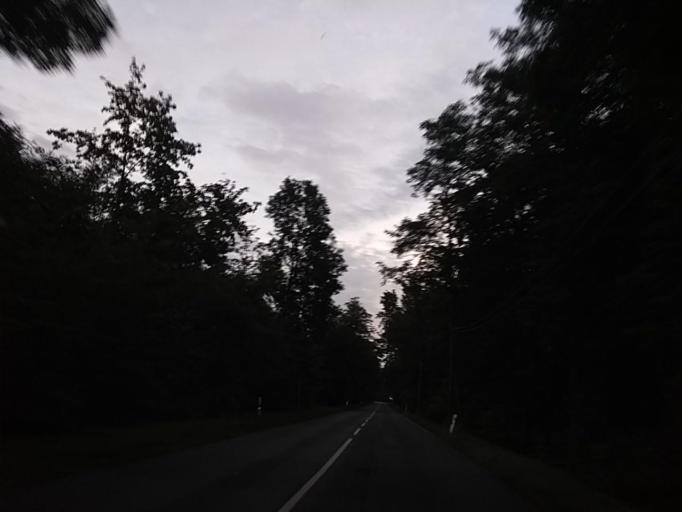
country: DE
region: Saxony-Anhalt
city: Theissen
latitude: 51.0975
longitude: 12.1329
